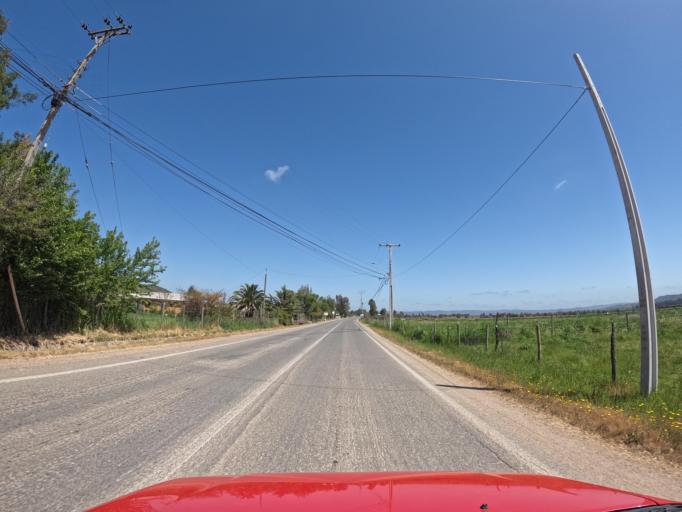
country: CL
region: O'Higgins
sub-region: Provincia de Colchagua
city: Santa Cruz
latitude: -34.7293
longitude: -71.6690
